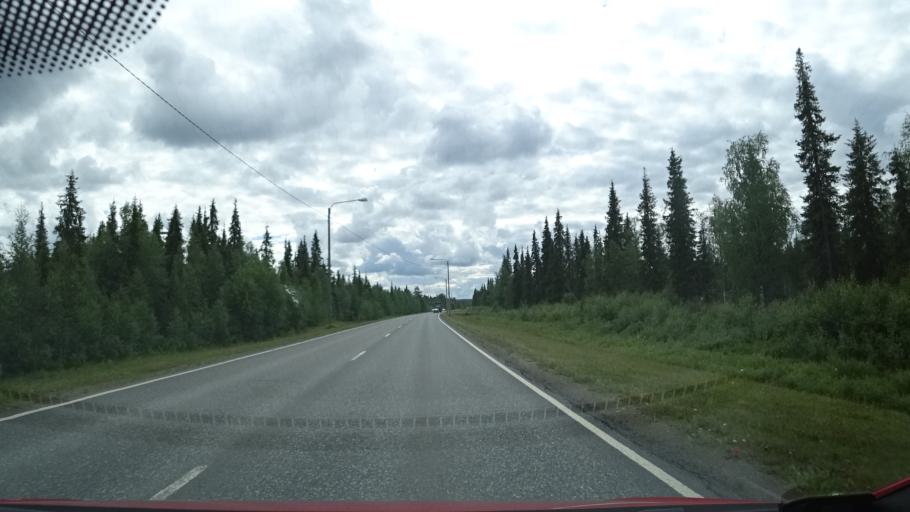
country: FI
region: Lapland
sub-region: Tunturi-Lappi
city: Kittilae
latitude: 67.6924
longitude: 24.8657
